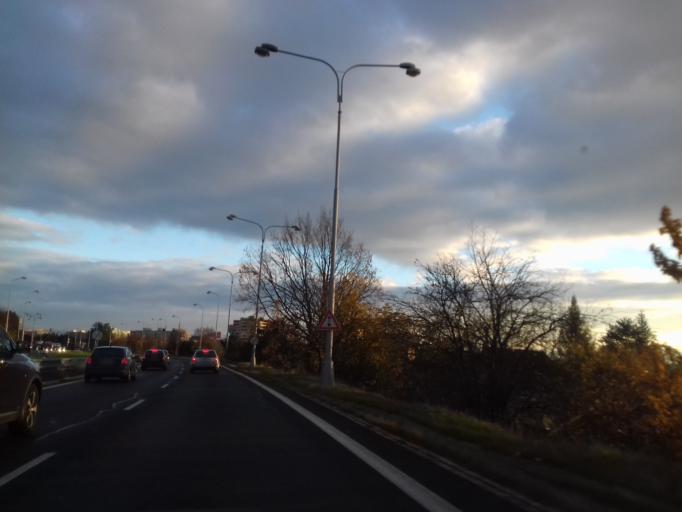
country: CZ
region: Olomoucky
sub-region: Okres Olomouc
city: Olomouc
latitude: 49.5744
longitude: 17.2357
